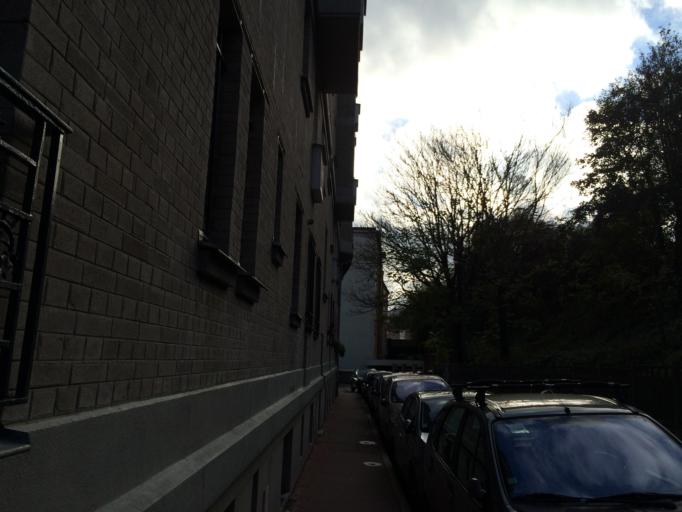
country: FR
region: Ile-de-France
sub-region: Departement des Hauts-de-Seine
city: Suresnes
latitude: 48.8645
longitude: 2.2186
